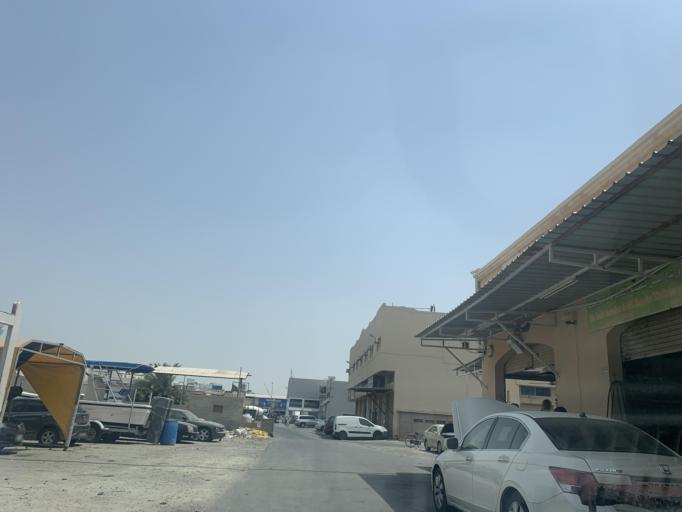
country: BH
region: Central Governorate
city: Madinat Hamad
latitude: 26.1424
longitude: 50.4893
